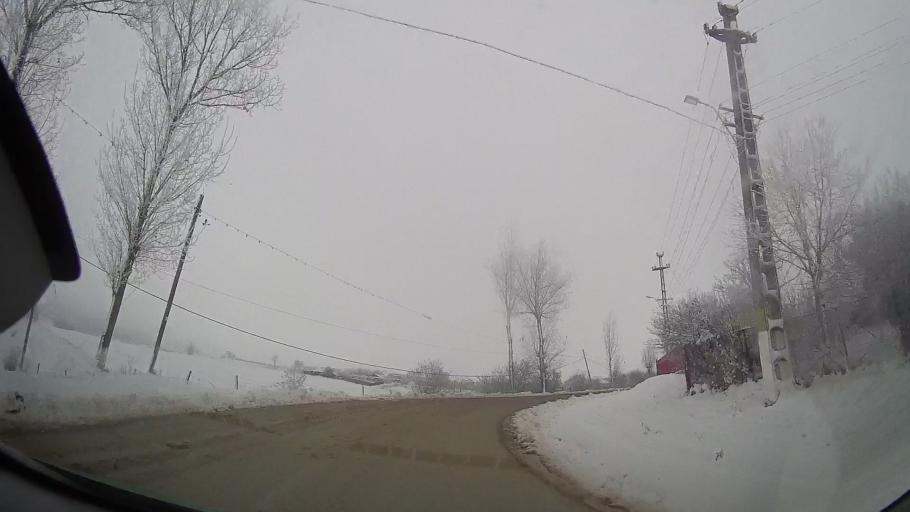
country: RO
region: Iasi
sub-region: Comuna Dagata
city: Dagata
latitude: 46.9150
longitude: 27.1988
